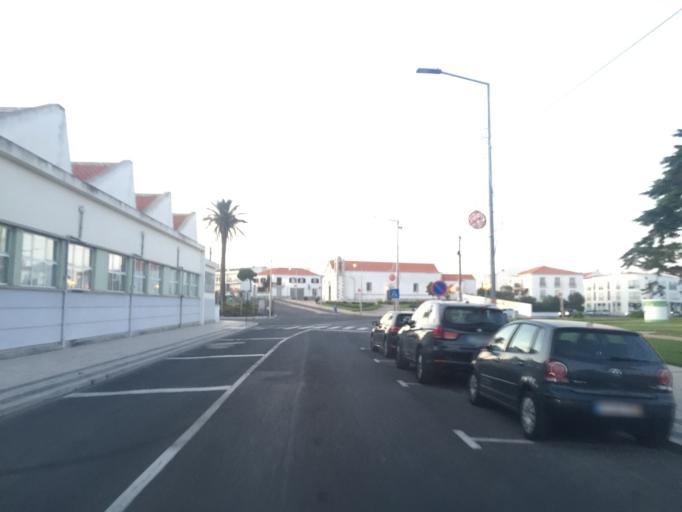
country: PT
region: Leiria
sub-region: Peniche
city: Peniche
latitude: 39.3638
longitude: -9.3787
